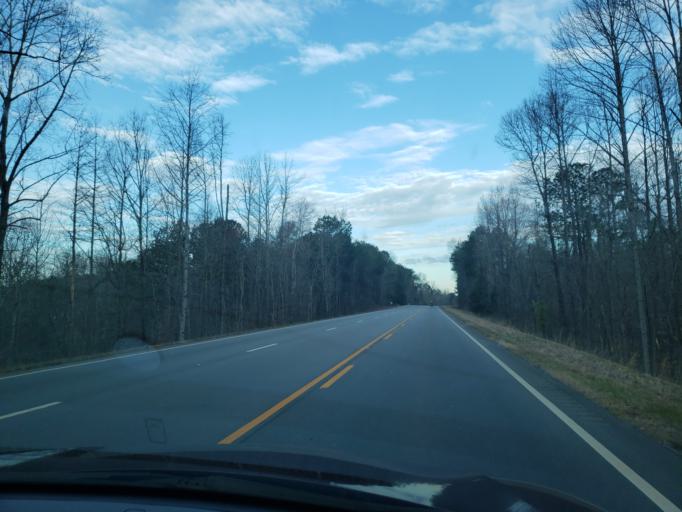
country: US
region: Alabama
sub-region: Randolph County
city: Roanoke
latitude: 33.2243
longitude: -85.4272
